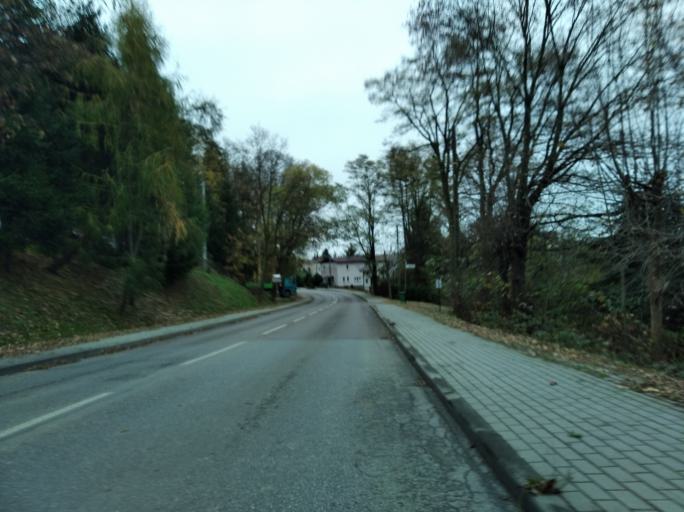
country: PL
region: Subcarpathian Voivodeship
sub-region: Krosno
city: Krosno
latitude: 49.7012
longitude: 21.7617
